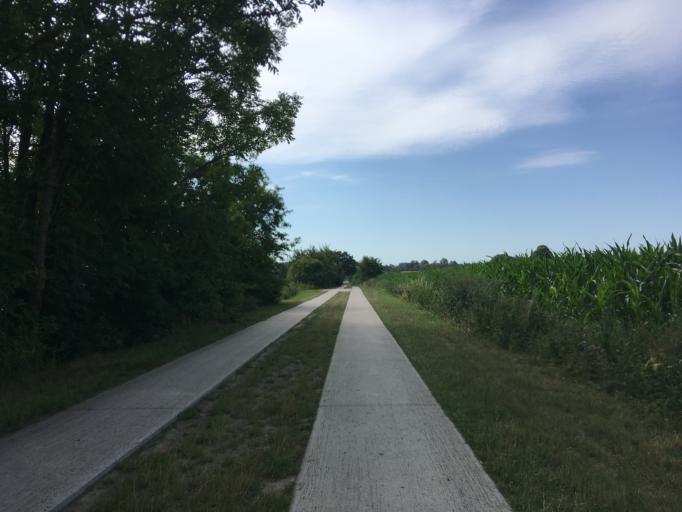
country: DE
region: Brandenburg
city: Zichow
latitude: 53.2175
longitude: 14.0435
